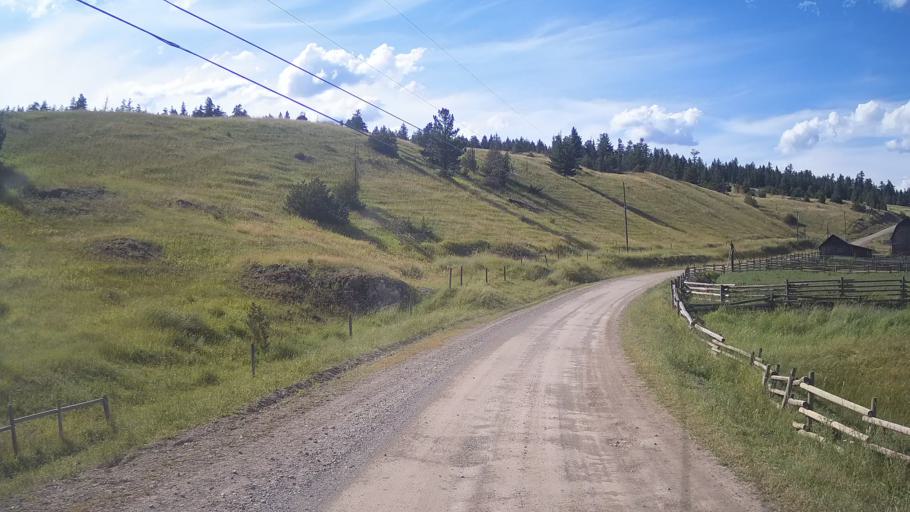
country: CA
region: British Columbia
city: Lillooet
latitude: 51.3034
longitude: -121.9858
